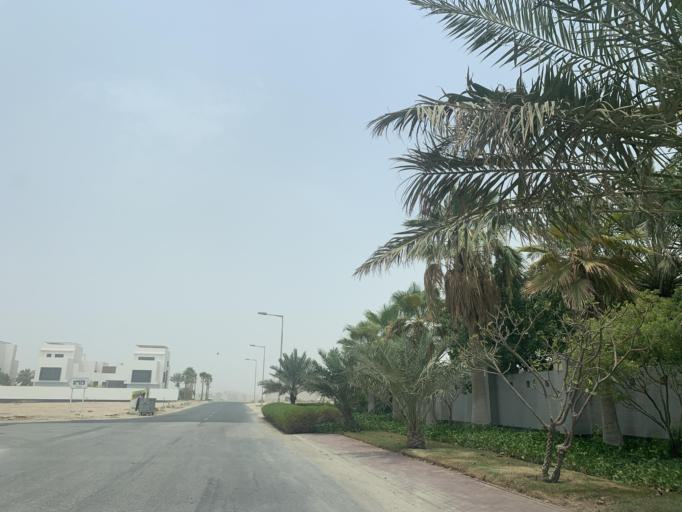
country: BH
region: Central Governorate
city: Madinat Hamad
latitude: 26.1686
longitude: 50.4764
